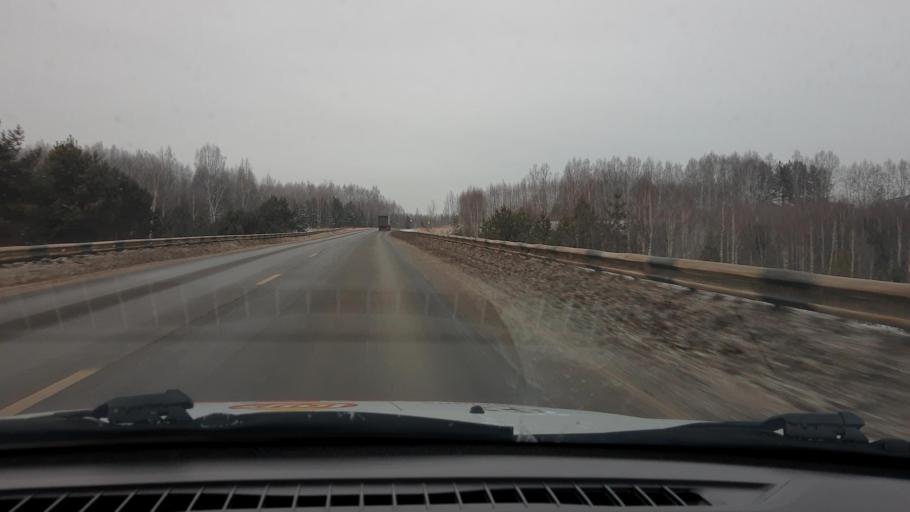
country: RU
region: Nizjnij Novgorod
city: Sitniki
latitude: 56.4794
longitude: 44.0247
